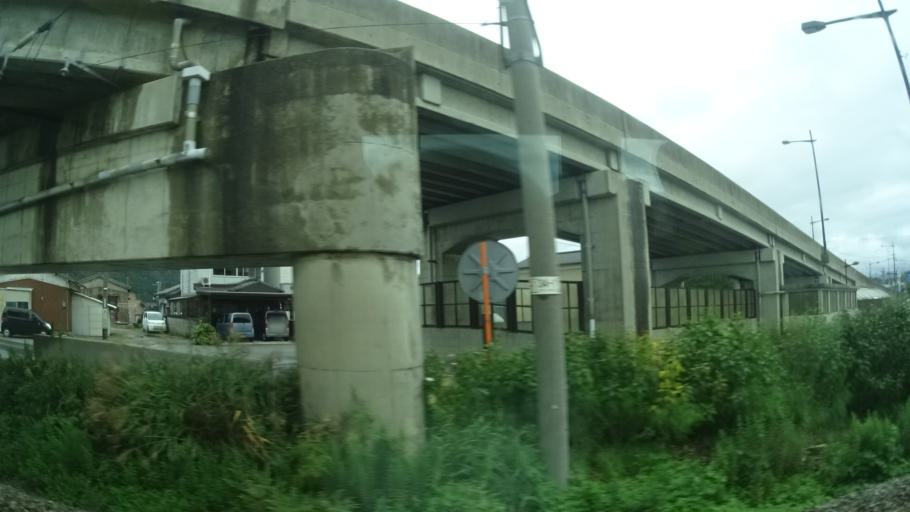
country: JP
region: Niigata
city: Murakami
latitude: 38.2259
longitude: 139.4632
